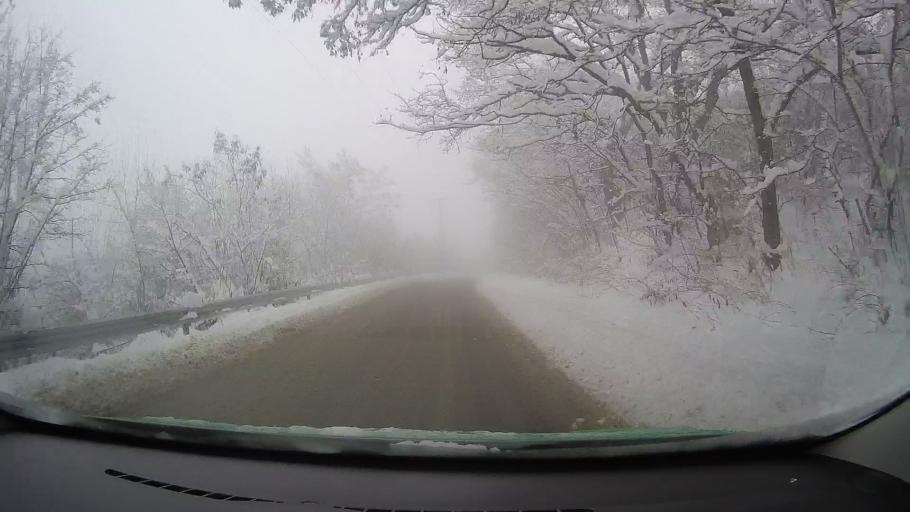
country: RO
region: Sibiu
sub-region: Comuna Poiana Sibiului
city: Poiana Sibiului
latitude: 45.8061
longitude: 23.7499
